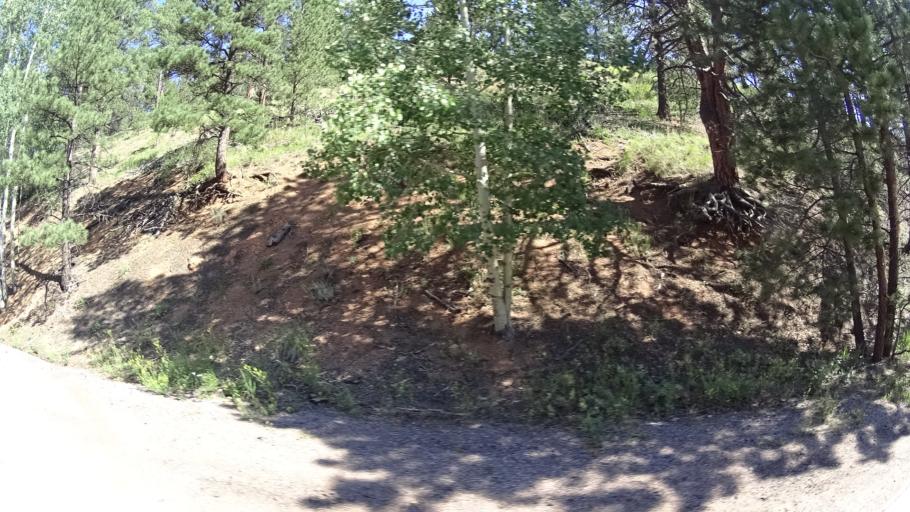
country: US
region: Colorado
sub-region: El Paso County
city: Cascade-Chipita Park
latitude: 38.9006
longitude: -104.9966
